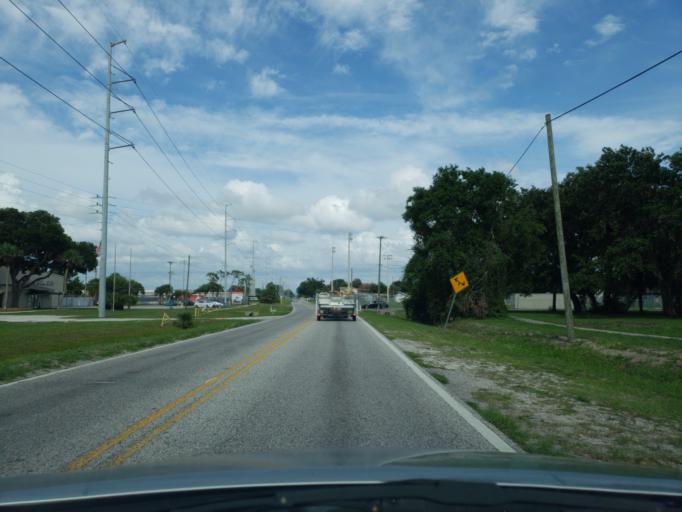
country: US
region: Florida
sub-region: Hillsborough County
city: Egypt Lake-Leto
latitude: 28.0108
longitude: -82.5252
